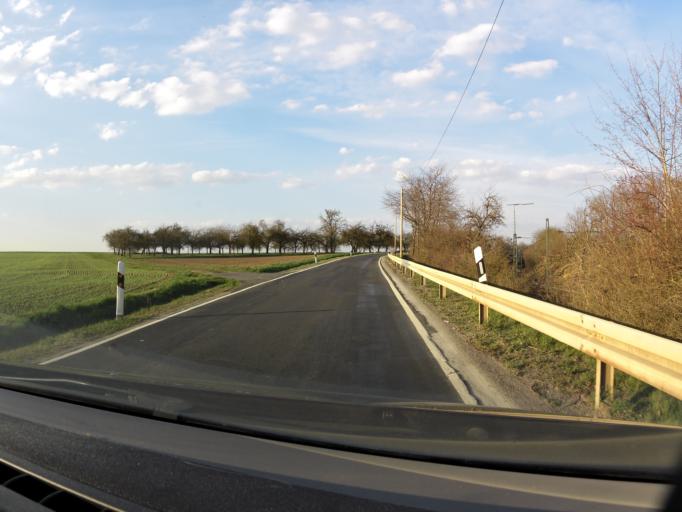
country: DE
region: Bavaria
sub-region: Regierungsbezirk Unterfranken
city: Geroldshausen
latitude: 49.6909
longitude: 9.9032
